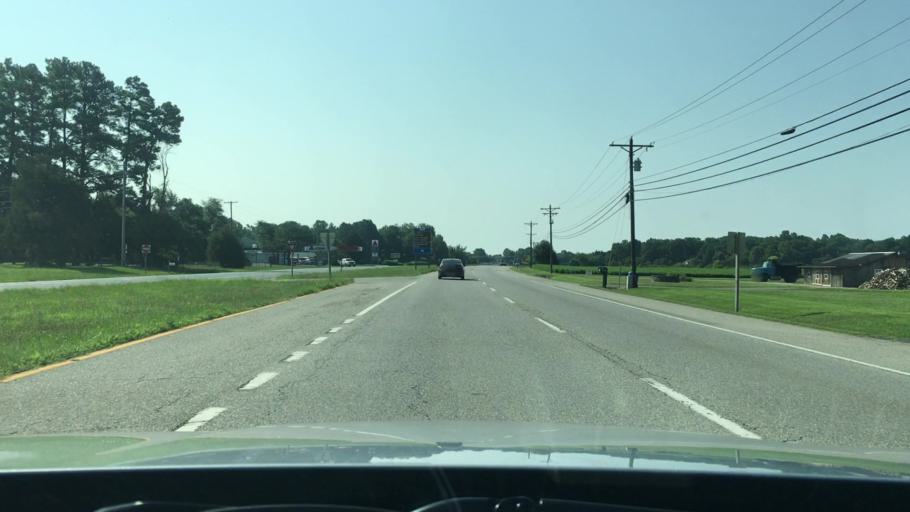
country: US
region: Maryland
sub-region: Charles County
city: La Plata
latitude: 38.4121
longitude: -76.9556
